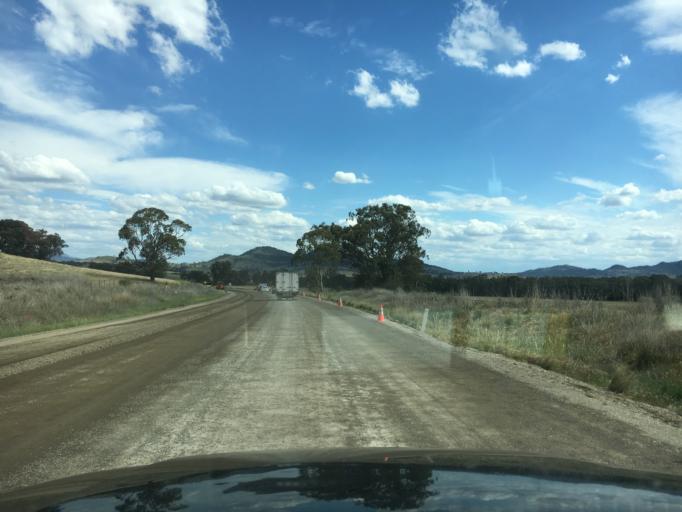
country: AU
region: New South Wales
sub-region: Liverpool Plains
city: Quirindi
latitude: -31.4538
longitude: 150.8613
